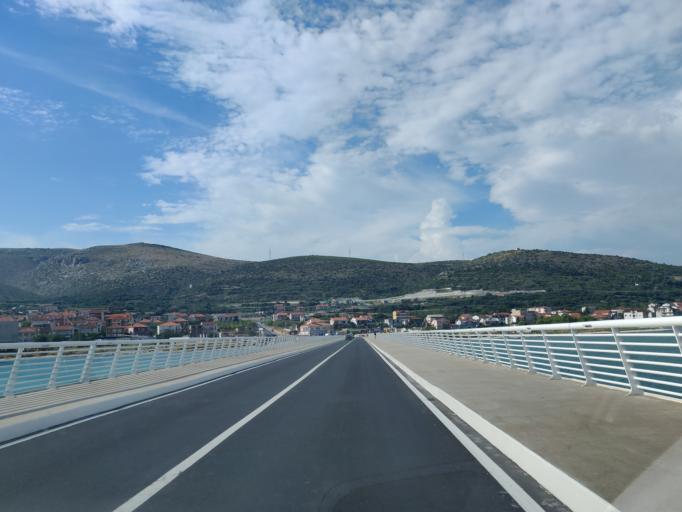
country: HR
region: Splitsko-Dalmatinska
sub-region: Grad Trogir
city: Trogir
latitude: 43.5189
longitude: 16.2650
